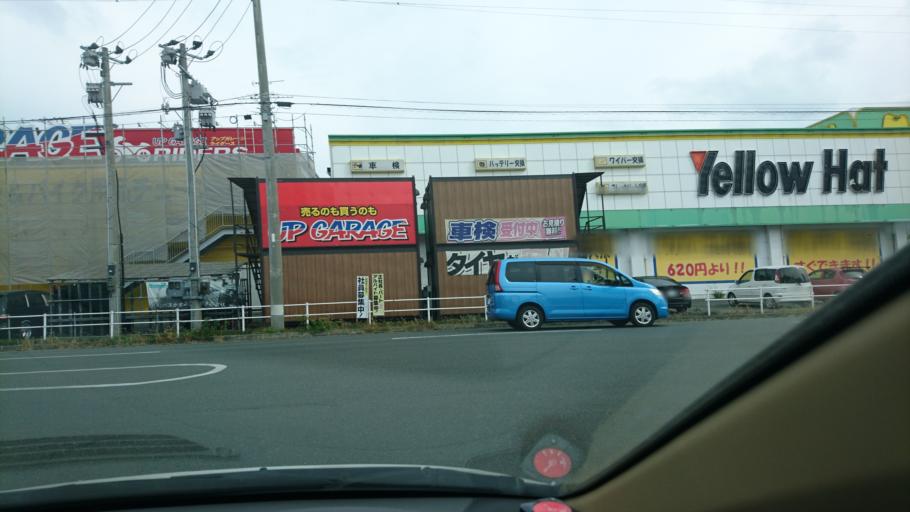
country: JP
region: Iwate
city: Morioka-shi
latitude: 39.7111
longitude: 141.1011
